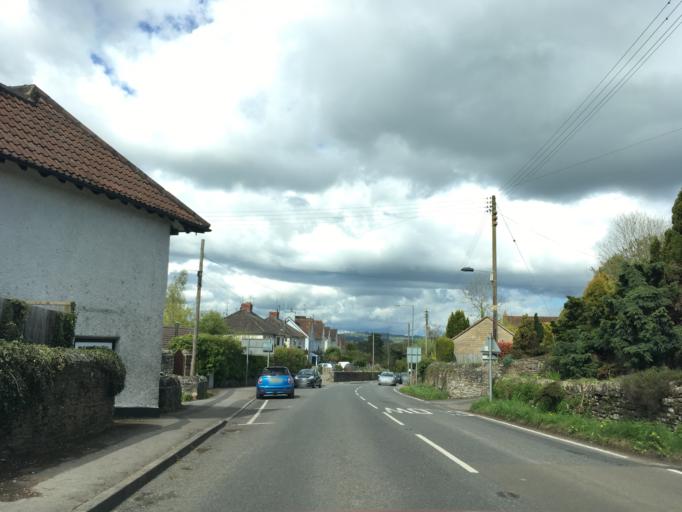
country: GB
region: England
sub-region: South Gloucestershire
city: Wickwar
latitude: 51.5971
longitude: -2.4000
